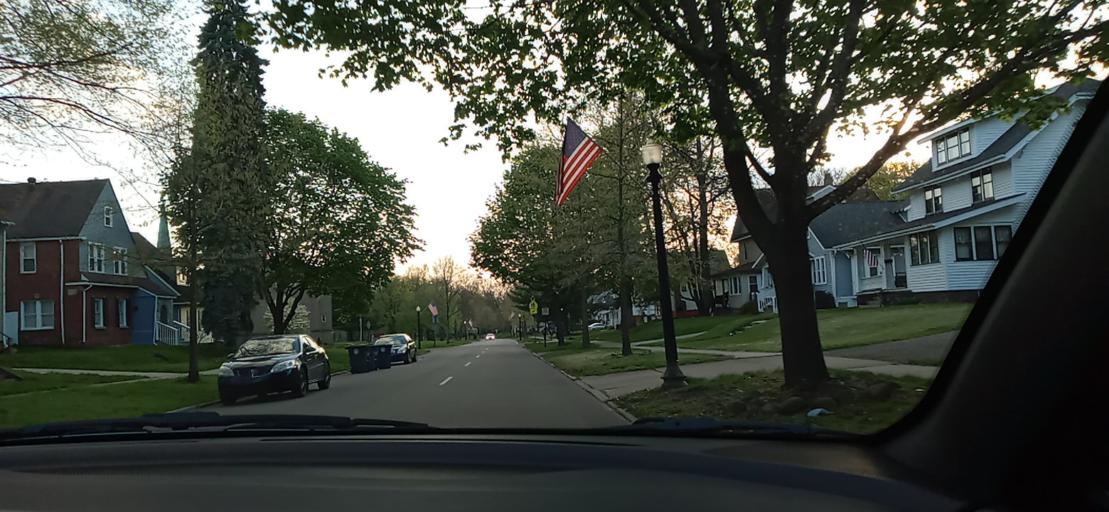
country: US
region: Ohio
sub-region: Summit County
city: Akron
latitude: 41.0443
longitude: -81.5157
